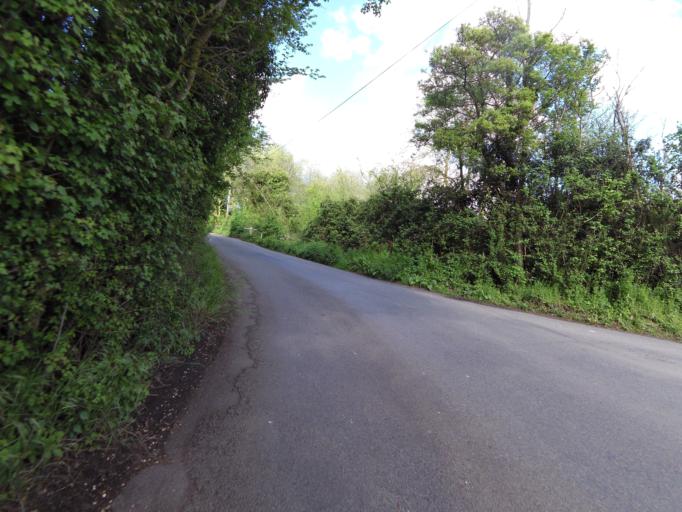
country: GB
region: England
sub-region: Suffolk
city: Woolpit
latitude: 52.2201
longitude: 0.8802
